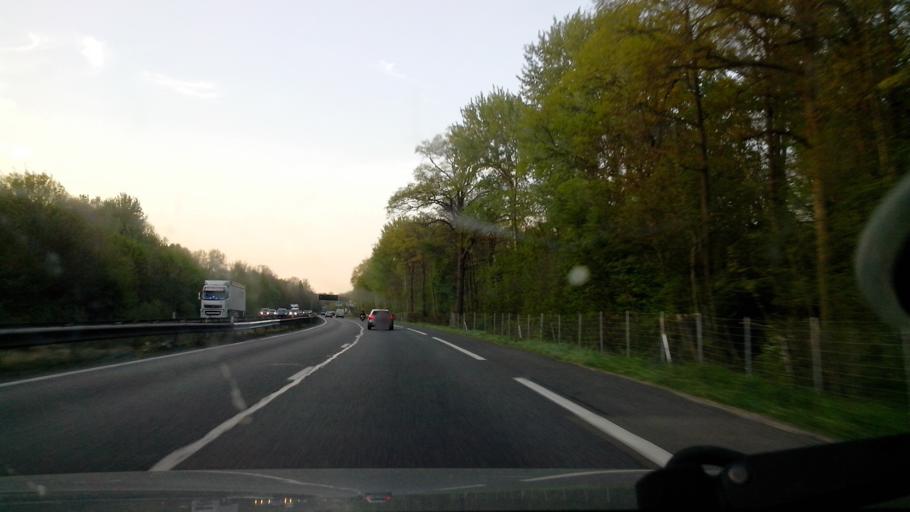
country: FR
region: Ile-de-France
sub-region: Departement de Seine-et-Marne
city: Lesigny
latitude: 48.7558
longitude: 2.6153
